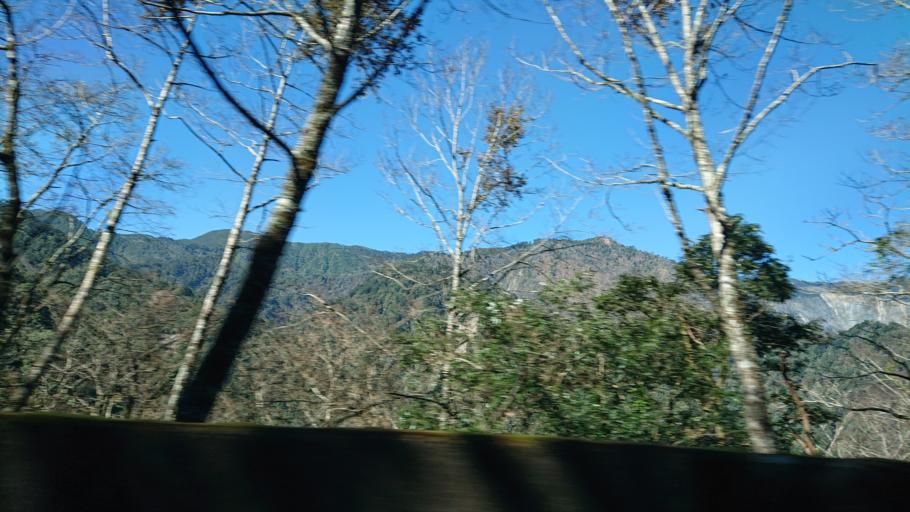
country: TW
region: Taiwan
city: Daxi
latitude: 24.4051
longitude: 121.3667
